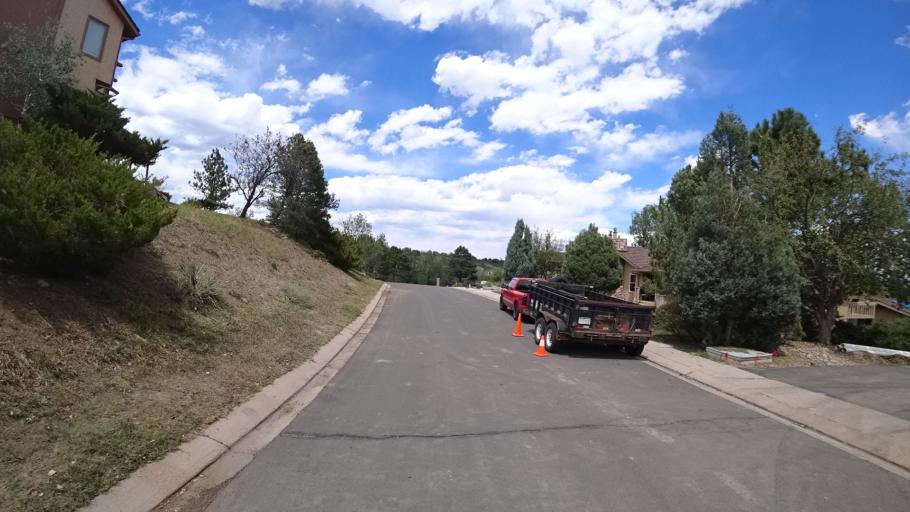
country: US
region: Colorado
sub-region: El Paso County
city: Stratmoor
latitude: 38.7750
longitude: -104.8345
